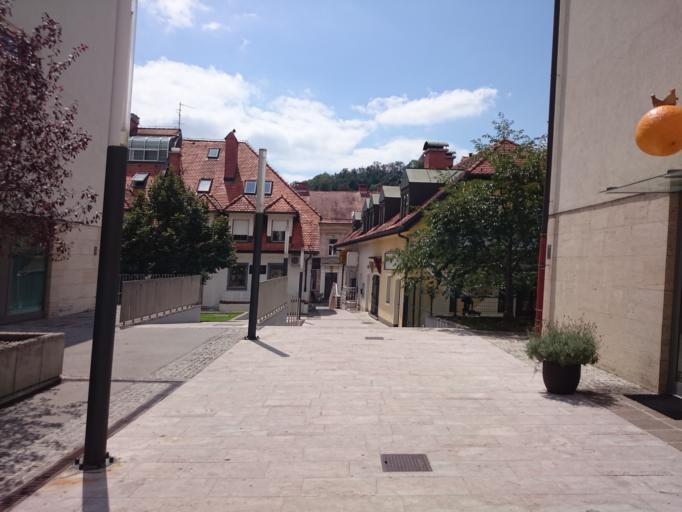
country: SI
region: Ljubljana
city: Ljubljana
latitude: 46.0529
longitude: 14.5116
